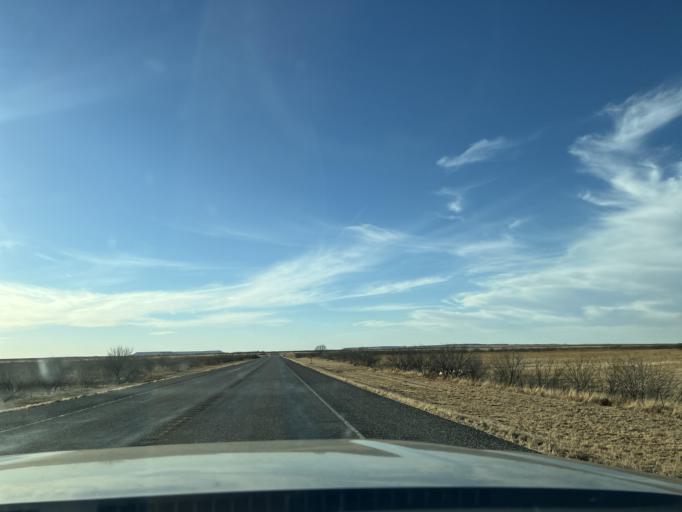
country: US
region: Texas
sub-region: Borden County
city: Gail
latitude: 32.7705
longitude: -101.3312
